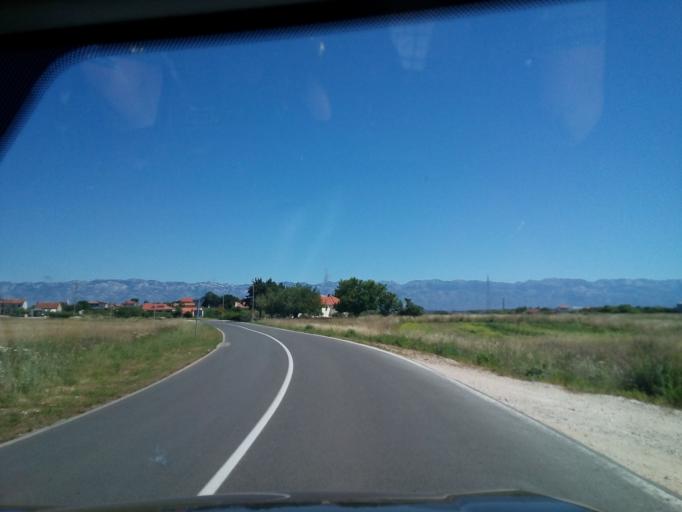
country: HR
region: Zadarska
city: Nin
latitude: 44.2332
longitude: 15.1815
